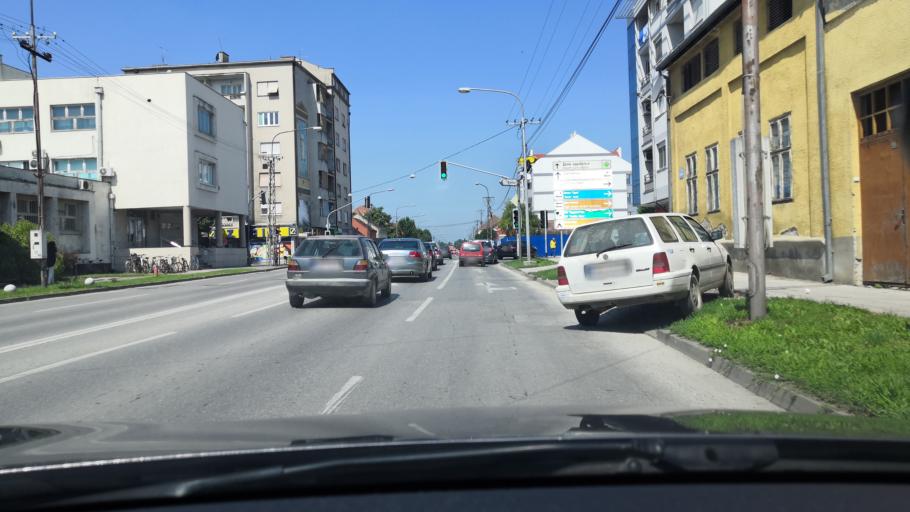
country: RS
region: Autonomna Pokrajina Vojvodina
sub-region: Sremski Okrug
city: Sremska Mitrovica
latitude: 44.9723
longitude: 19.6103
